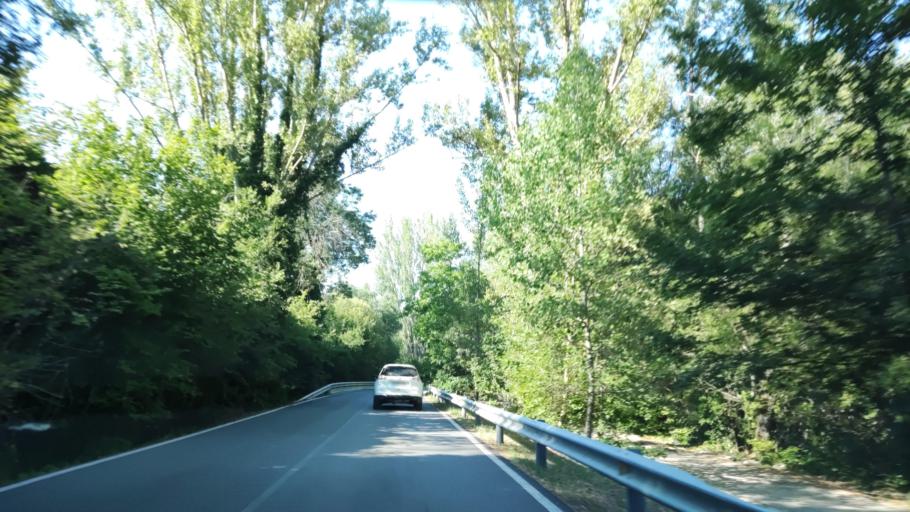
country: ES
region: Madrid
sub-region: Provincia de Madrid
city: Rascafria
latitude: 40.8908
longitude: -3.8848
